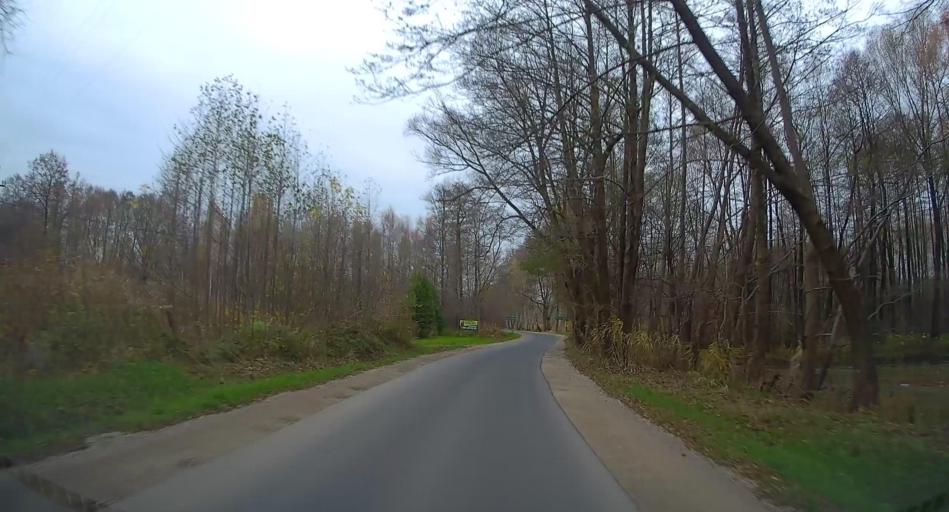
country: PL
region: Lodz Voivodeship
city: Zabia Wola
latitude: 52.0176
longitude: 20.6559
